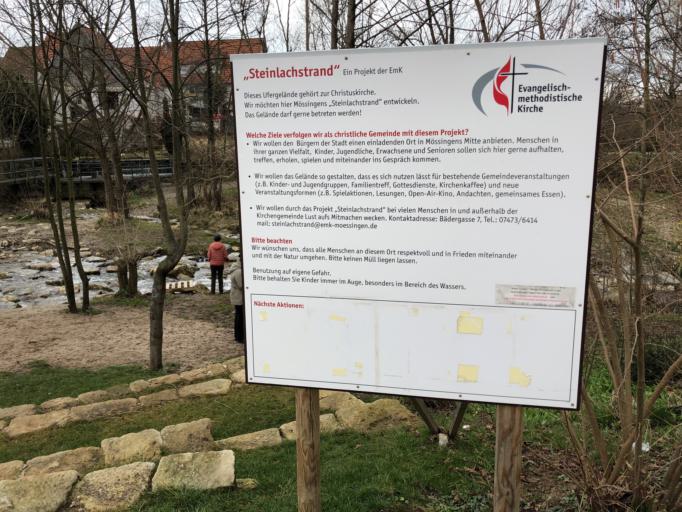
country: DE
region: Baden-Wuerttemberg
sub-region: Tuebingen Region
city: Mossingen
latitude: 48.4074
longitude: 9.0602
